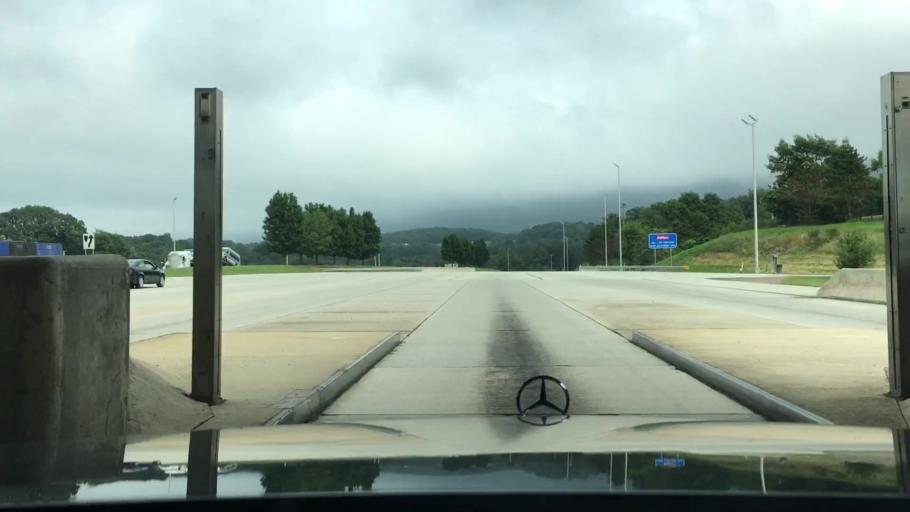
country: US
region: Pennsylvania
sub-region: Bedford County
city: Earlston
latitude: 39.9885
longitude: -78.2519
